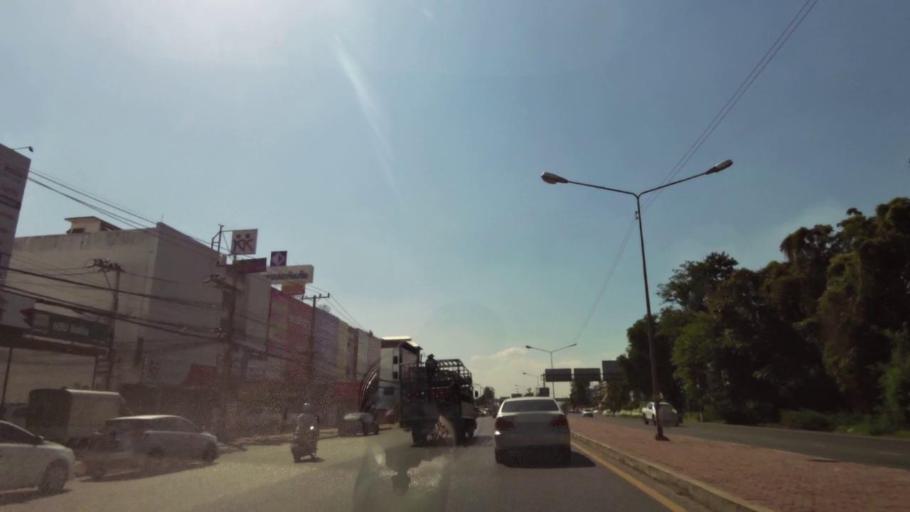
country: TH
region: Nakhon Sawan
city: Nakhon Sawan
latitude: 15.7098
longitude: 100.1168
